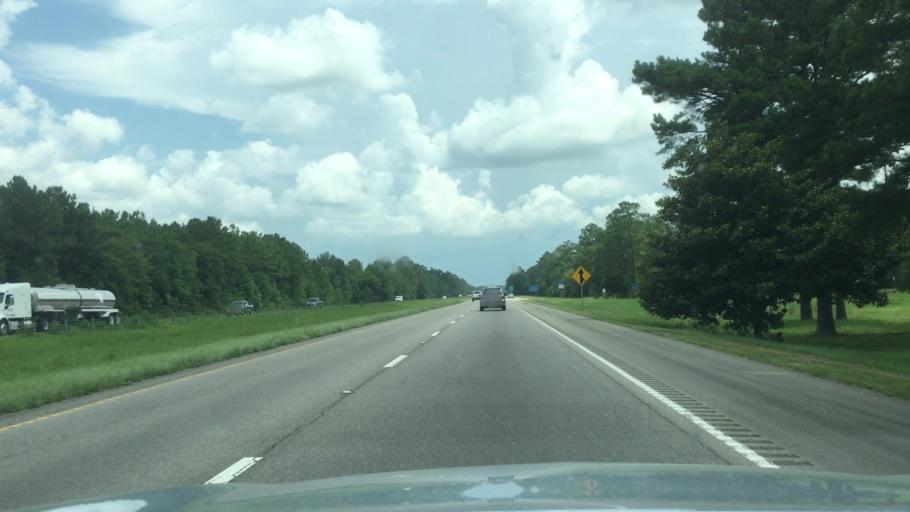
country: US
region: Mississippi
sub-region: Pearl River County
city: Picayune
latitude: 30.4988
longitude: -89.6697
